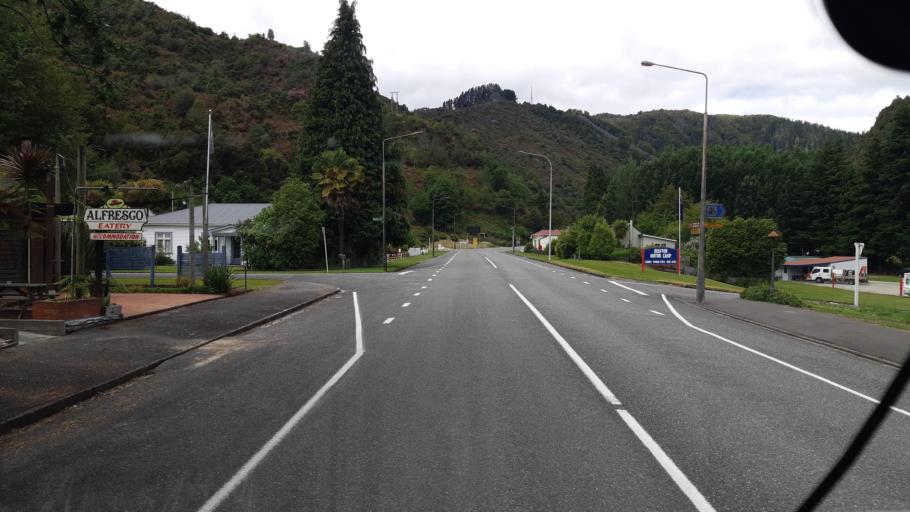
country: NZ
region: West Coast
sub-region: Buller District
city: Westport
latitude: -42.1198
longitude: 171.8689
